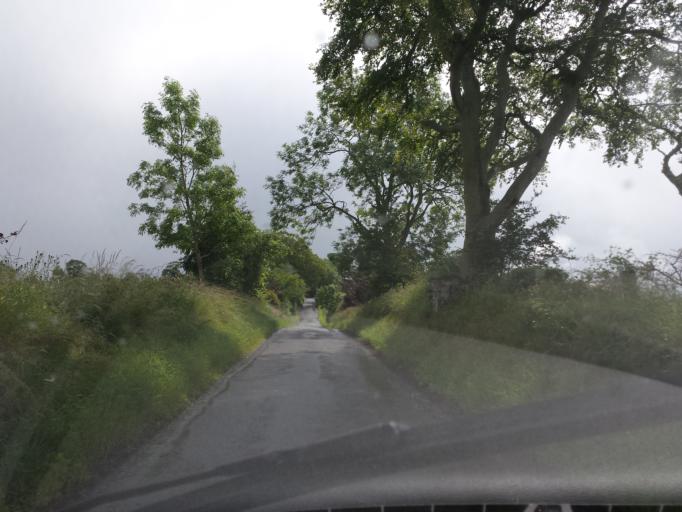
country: GB
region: Scotland
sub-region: The Scottish Borders
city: Saint Boswells
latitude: 55.5967
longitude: -2.6435
